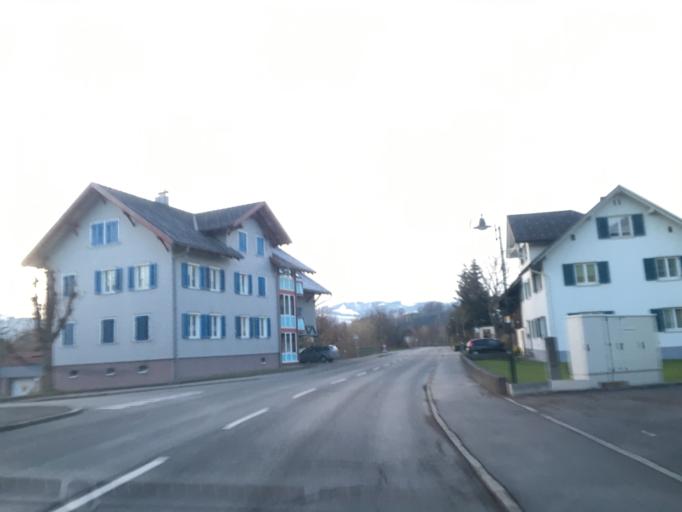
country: AT
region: Vorarlberg
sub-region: Politischer Bezirk Feldkirch
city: Koblach
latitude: 47.3311
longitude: 9.6006
